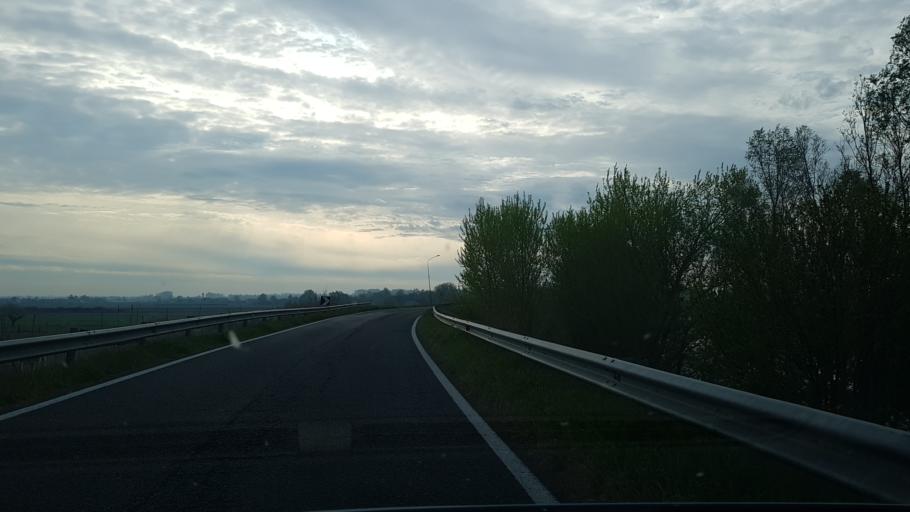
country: IT
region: Veneto
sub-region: Provincia di Rovigo
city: Lusia
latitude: 45.1070
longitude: 11.6691
